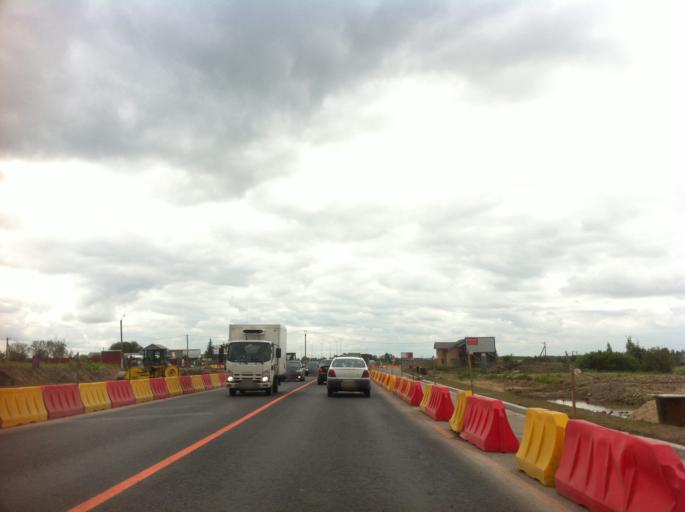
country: RU
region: Leningrad
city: Maloye Verevo
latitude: 59.6730
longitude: 30.2349
